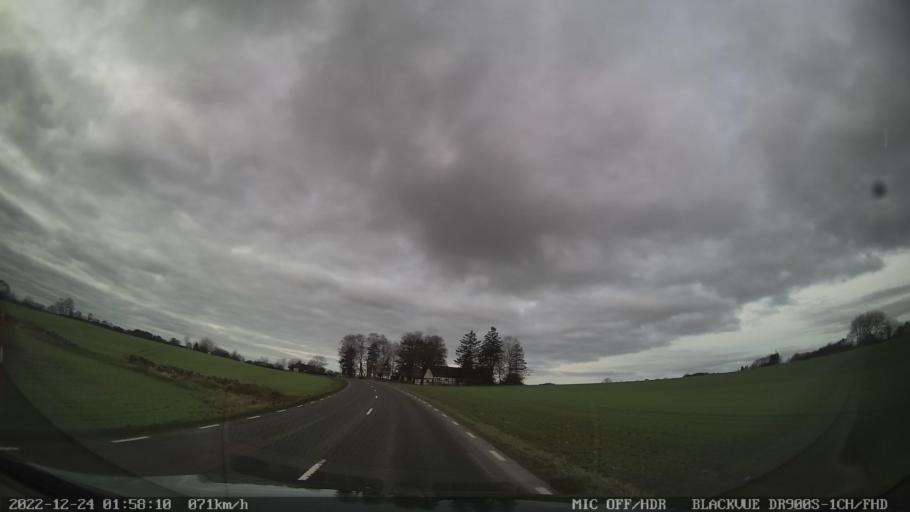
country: SE
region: Skane
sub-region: Tomelilla Kommun
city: Tomelilla
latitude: 55.6024
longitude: 14.0370
